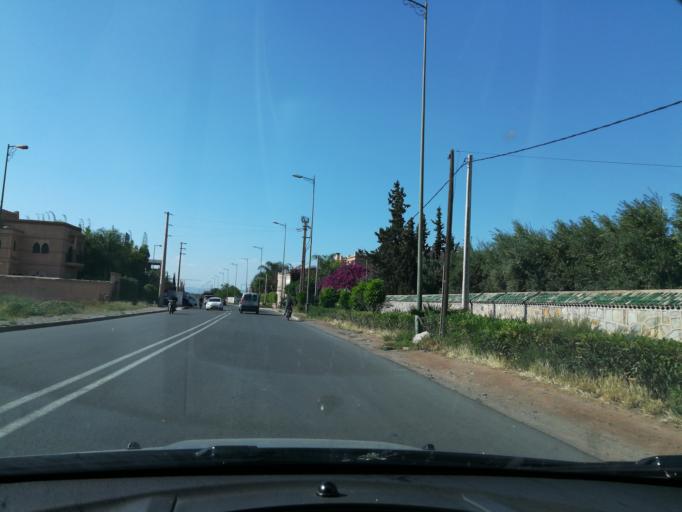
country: MA
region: Marrakech-Tensift-Al Haouz
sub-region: Marrakech
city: Marrakesh
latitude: 31.6605
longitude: -8.0546
